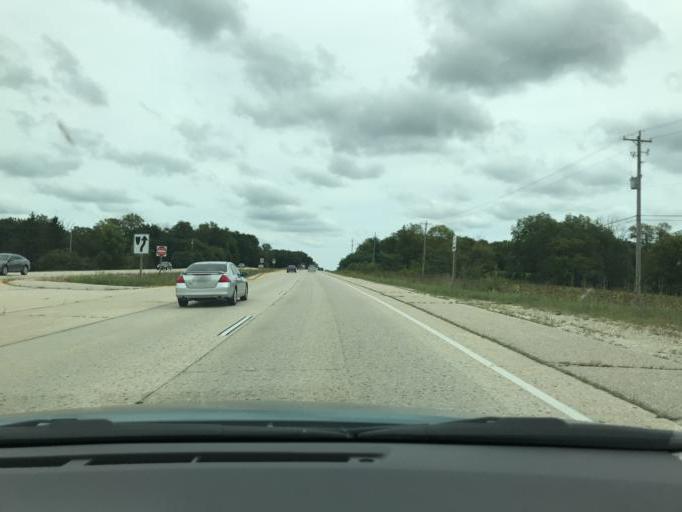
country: US
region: Wisconsin
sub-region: Kenosha County
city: Bristol
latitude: 42.5680
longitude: -88.0629
